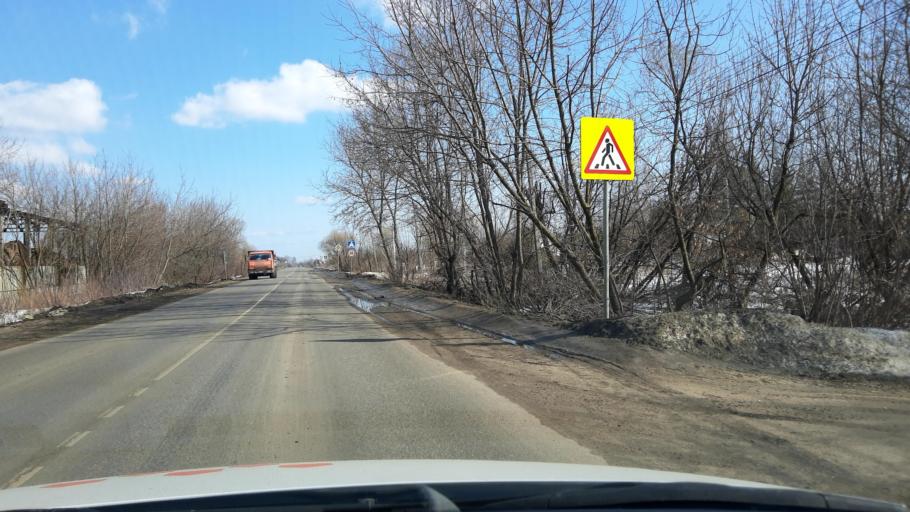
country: RU
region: Moskovskaya
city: Obukhovo
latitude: 55.8122
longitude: 38.3098
